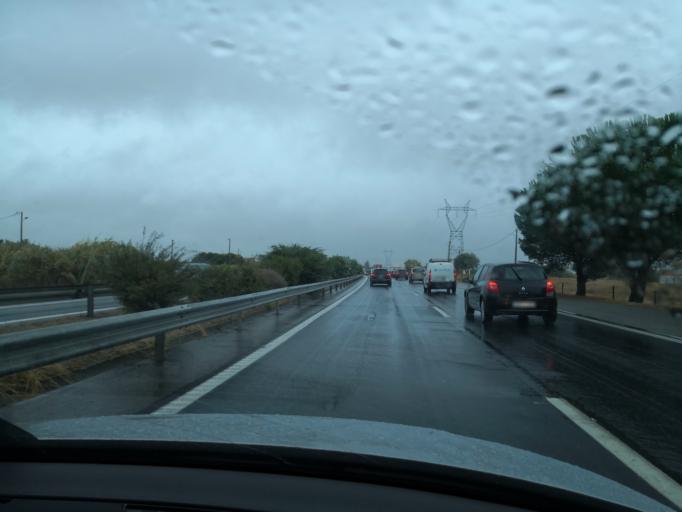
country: PT
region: Setubal
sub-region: Moita
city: Moita
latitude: 38.6669
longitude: -8.9545
